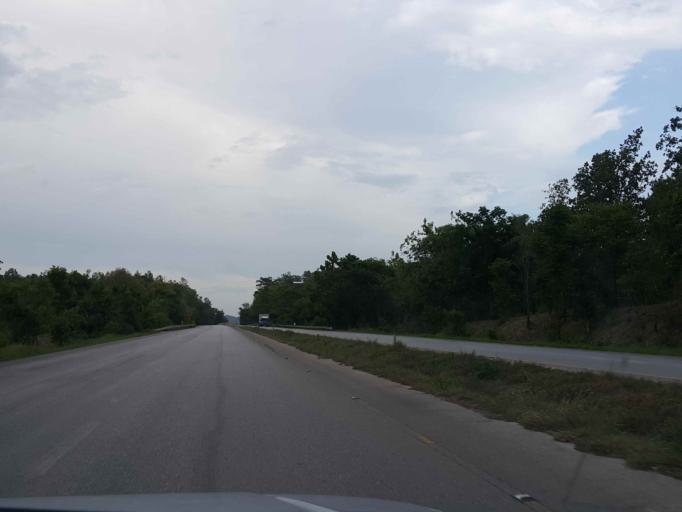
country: TH
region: Lampang
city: Soem Ngam
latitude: 18.0395
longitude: 99.3782
